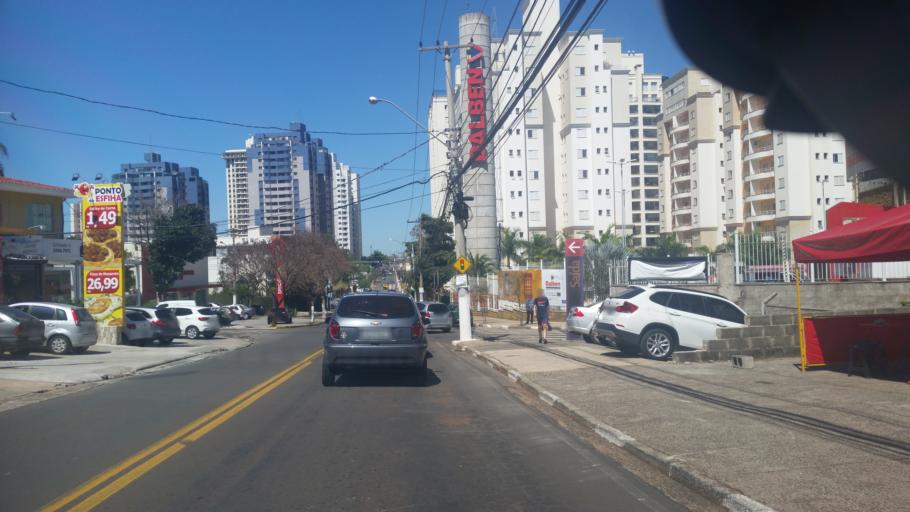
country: BR
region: Sao Paulo
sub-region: Campinas
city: Campinas
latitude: -22.8501
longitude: -47.0537
